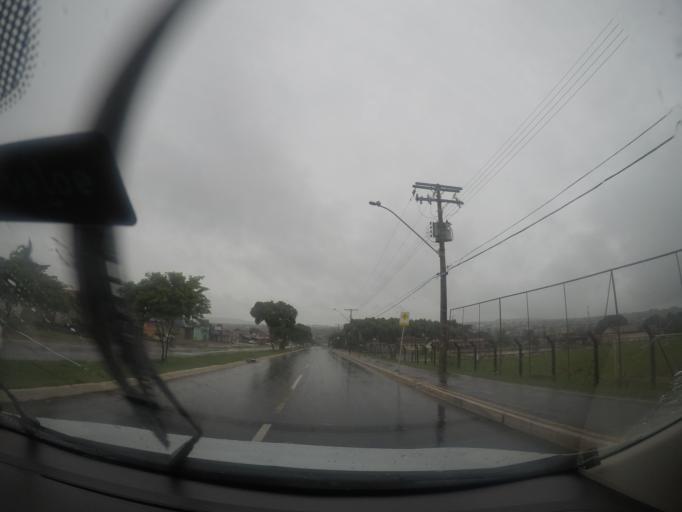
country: BR
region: Goias
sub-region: Goiania
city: Goiania
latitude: -16.6089
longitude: -49.3361
